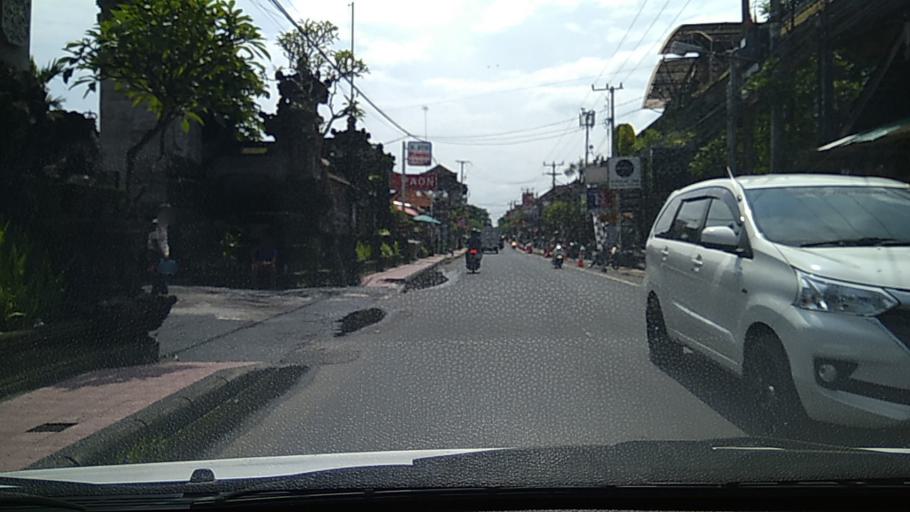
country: ID
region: Bali
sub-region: Kabupaten Gianyar
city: Ubud
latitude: -8.5058
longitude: 115.2601
